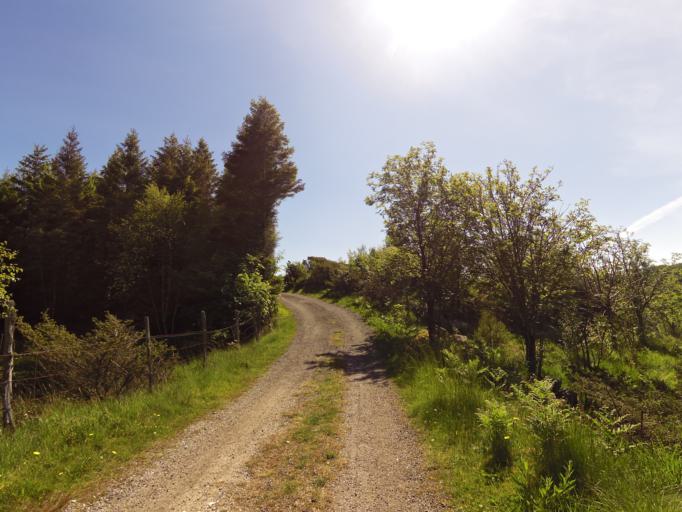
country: NO
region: Rogaland
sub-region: Eigersund
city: Egersund
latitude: 58.5031
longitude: 5.8981
